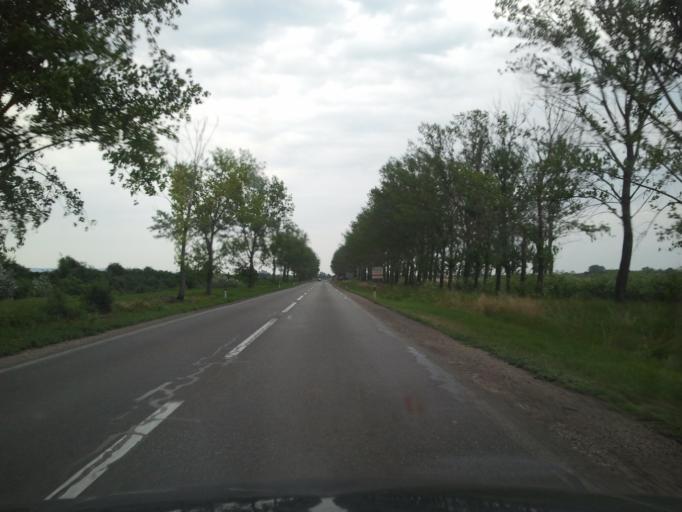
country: RS
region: Autonomna Pokrajina Vojvodina
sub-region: Sremski Okrug
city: Ruma
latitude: 44.9772
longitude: 19.8131
